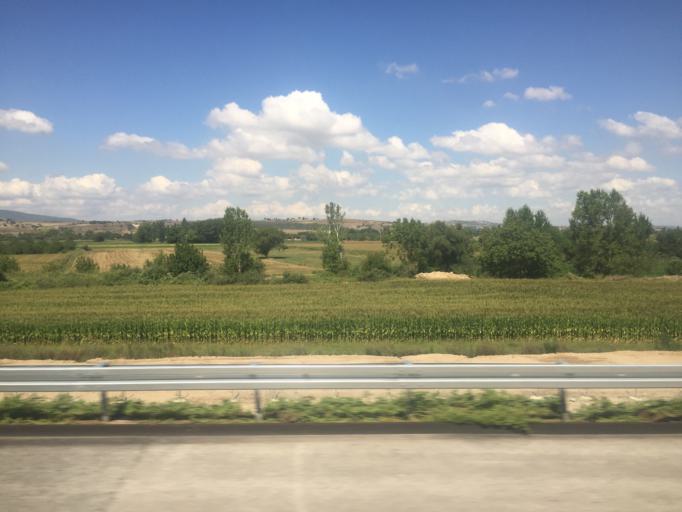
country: TR
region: Balikesir
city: Gobel
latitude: 39.9904
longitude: 28.1879
